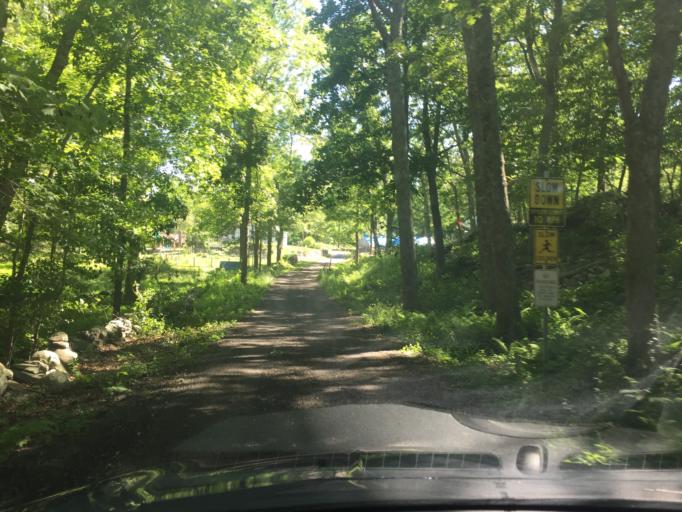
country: US
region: Rhode Island
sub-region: Washington County
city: Hopkinton
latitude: 41.5106
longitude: -71.8022
